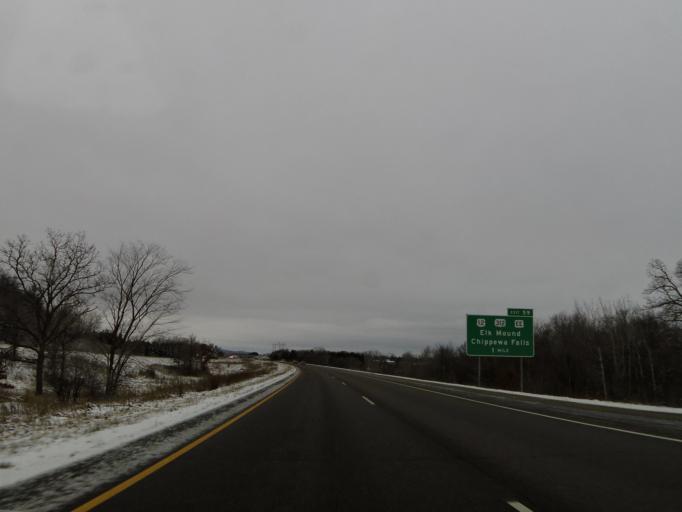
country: US
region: Wisconsin
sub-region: Eau Claire County
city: Eau Claire
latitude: 44.8318
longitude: -91.5792
